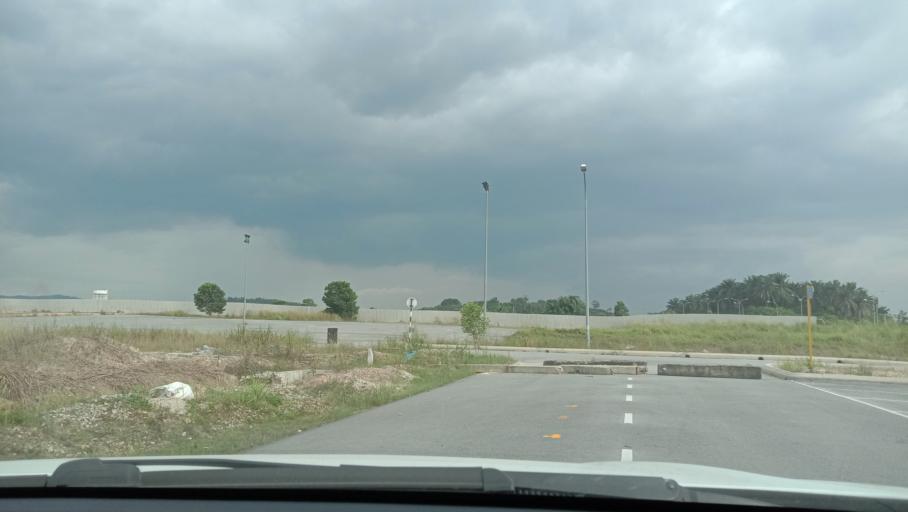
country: MY
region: Selangor
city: Ladang Seri Kundang
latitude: 3.2417
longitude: 101.4757
